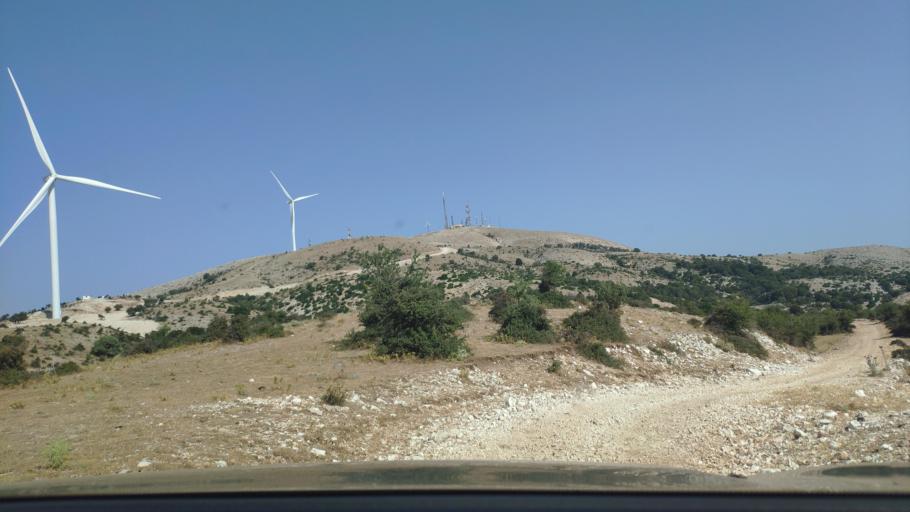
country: GR
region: West Greece
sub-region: Nomos Aitolias kai Akarnanias
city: Monastirakion
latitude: 38.7972
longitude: 20.9981
